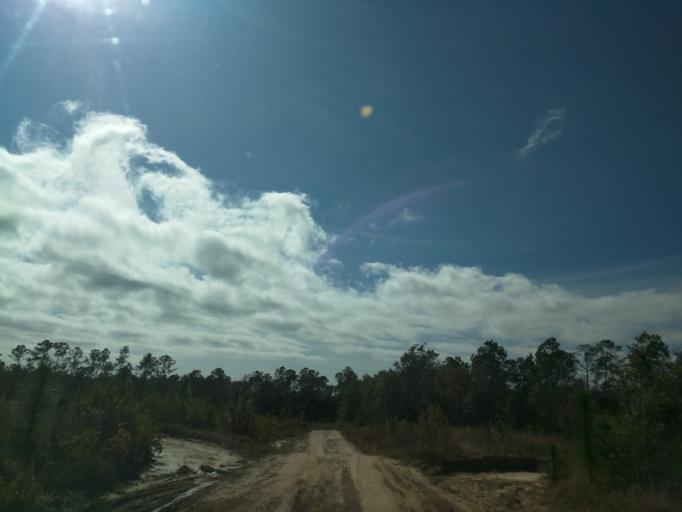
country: US
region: Florida
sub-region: Escambia County
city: Cantonment
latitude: 30.5499
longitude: -87.4271
